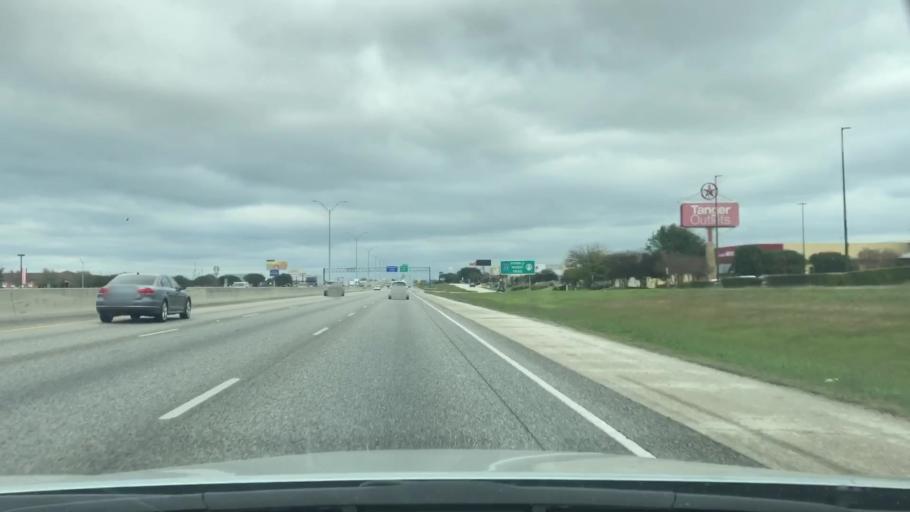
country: US
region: Texas
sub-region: Hays County
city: San Marcos
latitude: 29.8226
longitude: -97.9903
